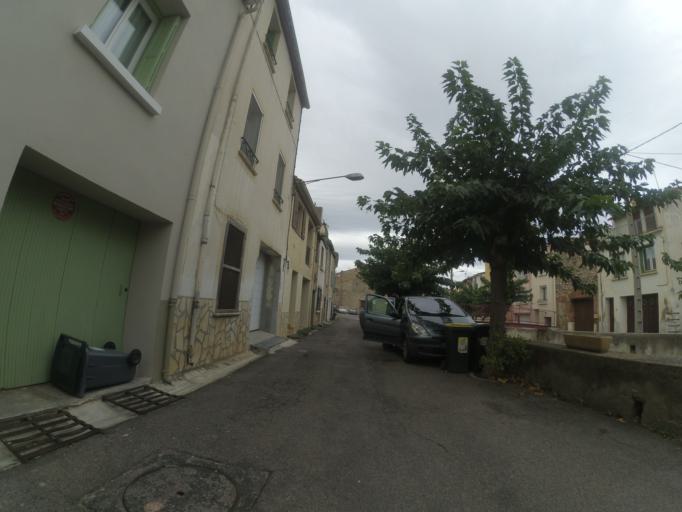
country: FR
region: Languedoc-Roussillon
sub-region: Departement des Pyrenees-Orientales
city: Estagel
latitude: 42.7712
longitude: 2.7010
